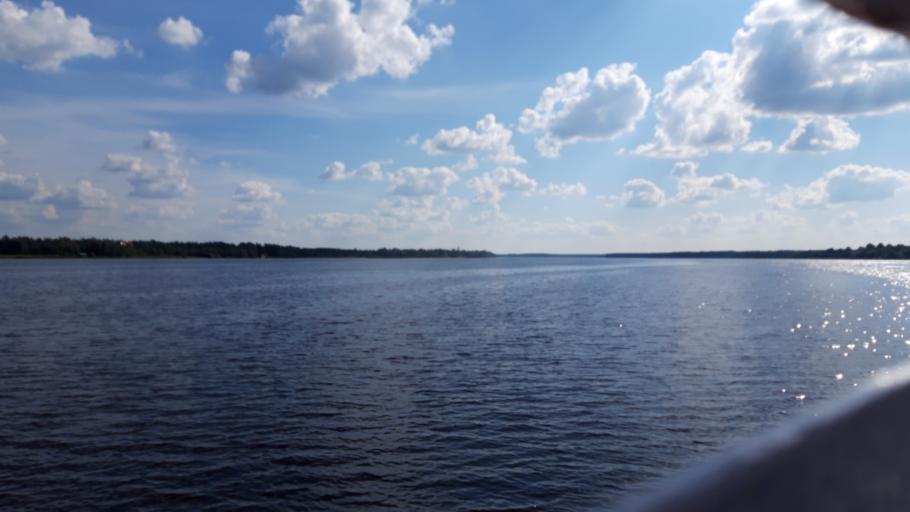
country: RU
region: Tverskaya
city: Konakovo
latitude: 56.6554
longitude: 36.6334
